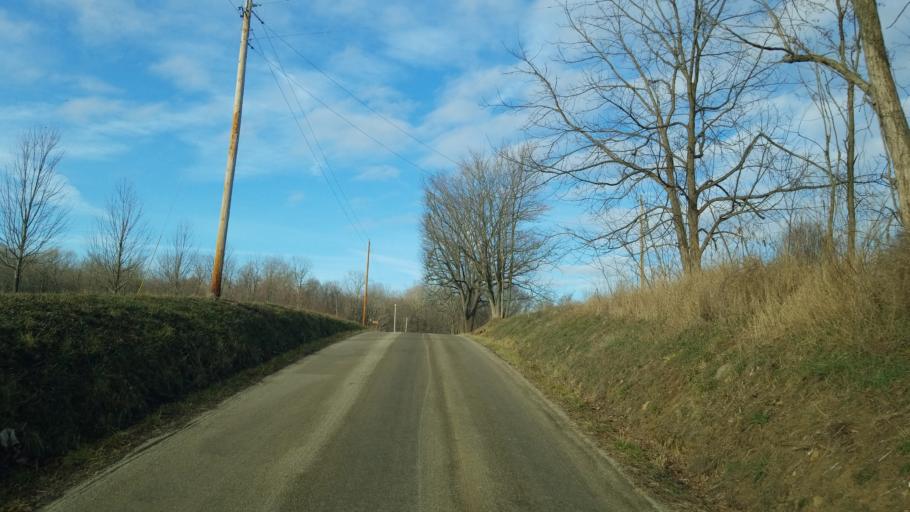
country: US
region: Ohio
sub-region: Knox County
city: Gambier
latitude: 40.3239
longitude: -82.3757
